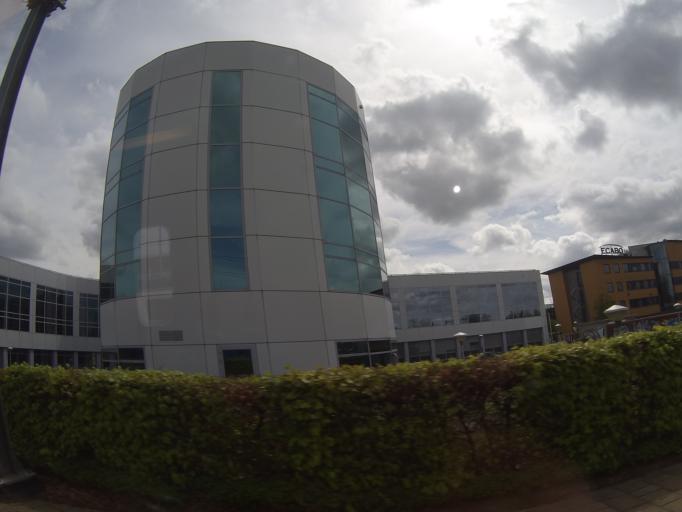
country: NL
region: Utrecht
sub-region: Gemeente Amersfoort
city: Amersfoort
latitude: 52.1744
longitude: 5.4033
